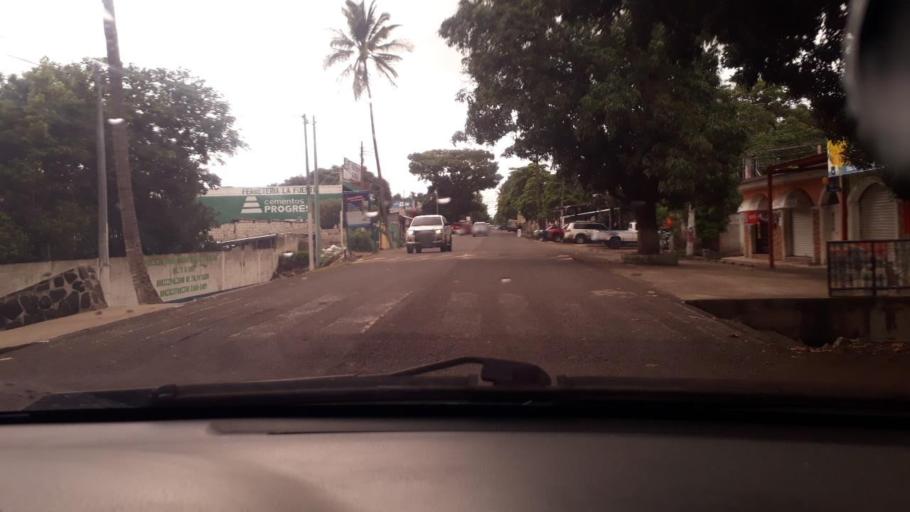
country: GT
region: Jutiapa
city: Jalpatagua
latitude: 14.1344
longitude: -90.0082
